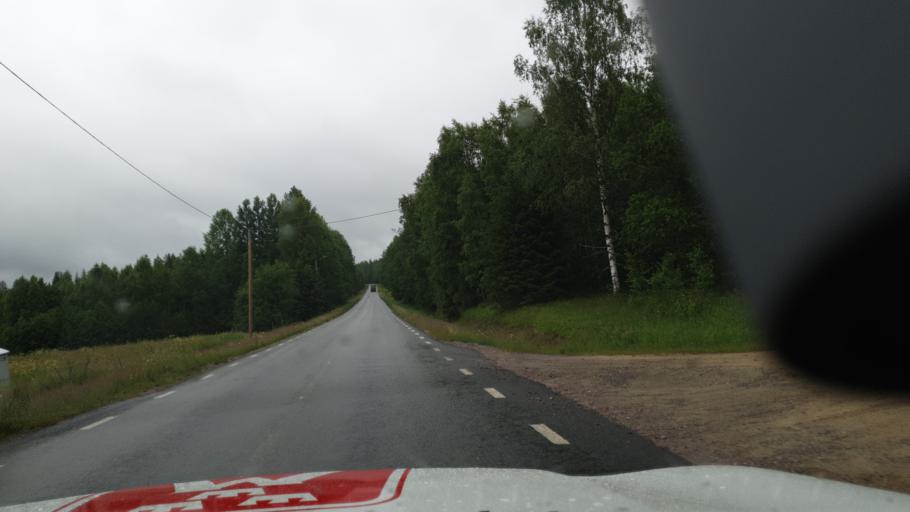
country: SE
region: Vaesterbotten
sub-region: Vannas Kommun
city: Vannasby
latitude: 63.8377
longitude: 19.8578
